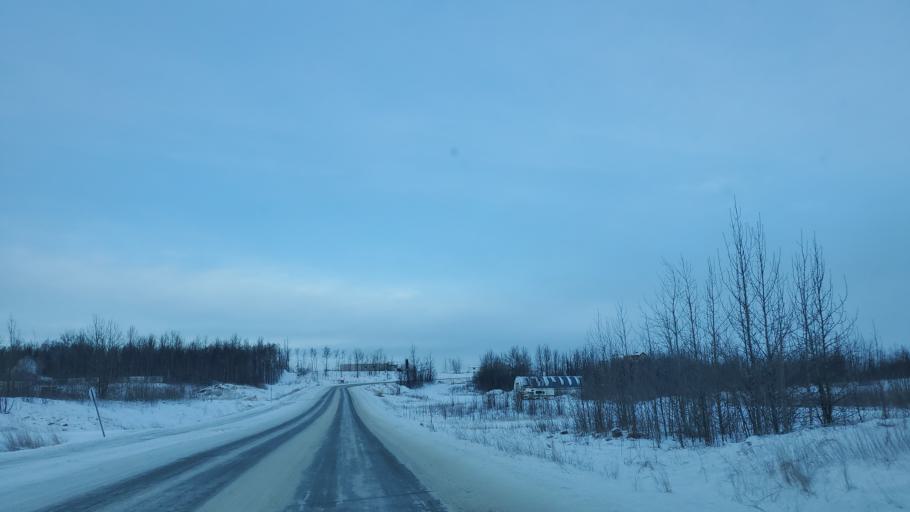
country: US
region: Alaska
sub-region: Matanuska-Susitna Borough
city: Gateway
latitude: 61.5572
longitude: -149.2723
